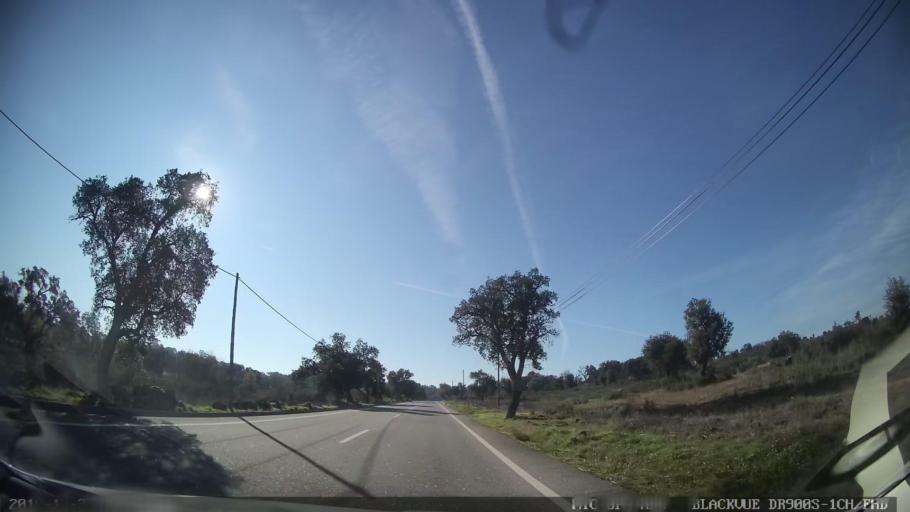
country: PT
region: Guarda
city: Alcains
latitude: 39.9555
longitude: -7.3718
